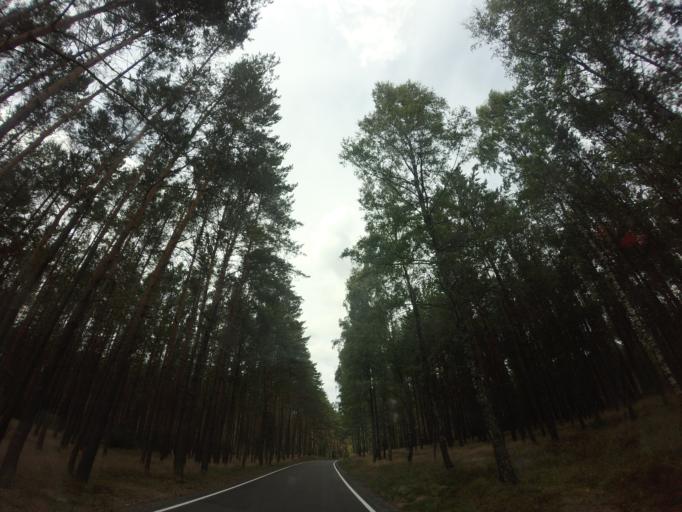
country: PL
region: West Pomeranian Voivodeship
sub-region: Powiat choszczenski
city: Drawno
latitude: 53.1274
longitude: 15.7279
